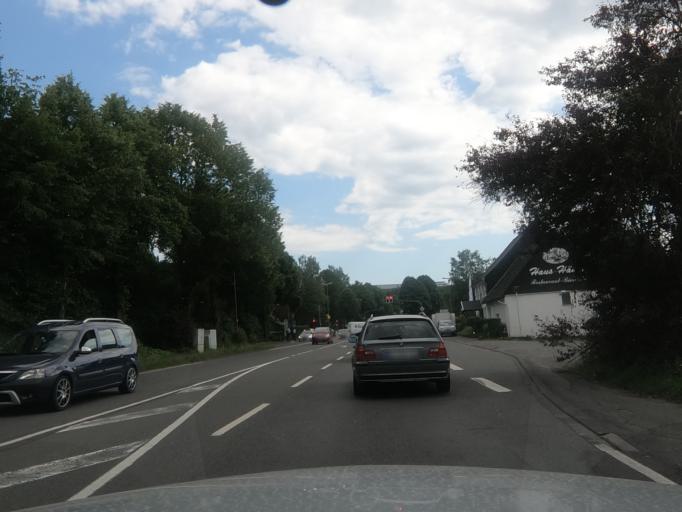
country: DE
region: North Rhine-Westphalia
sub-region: Regierungsbezirk Arnsberg
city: Olpe
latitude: 51.0047
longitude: 7.8414
